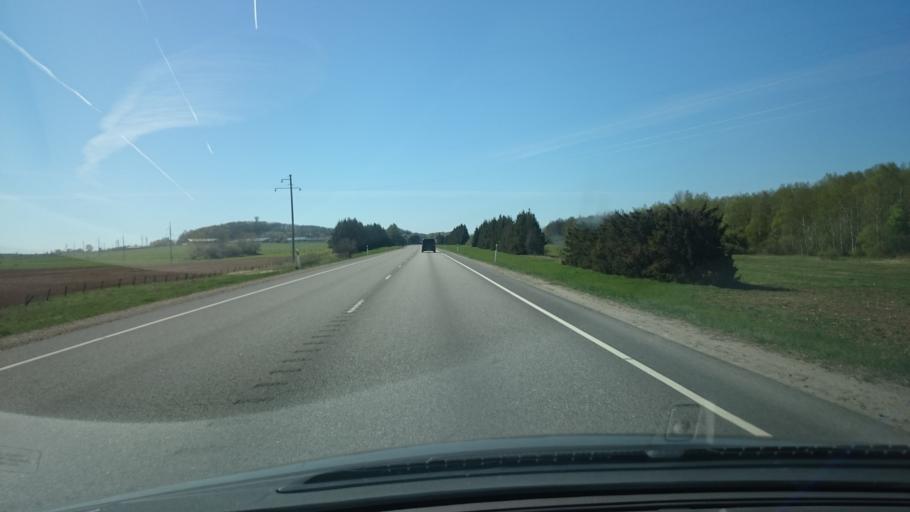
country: EE
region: Ida-Virumaa
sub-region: Sillamaee linn
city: Sillamae
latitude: 59.3770
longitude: 27.9071
